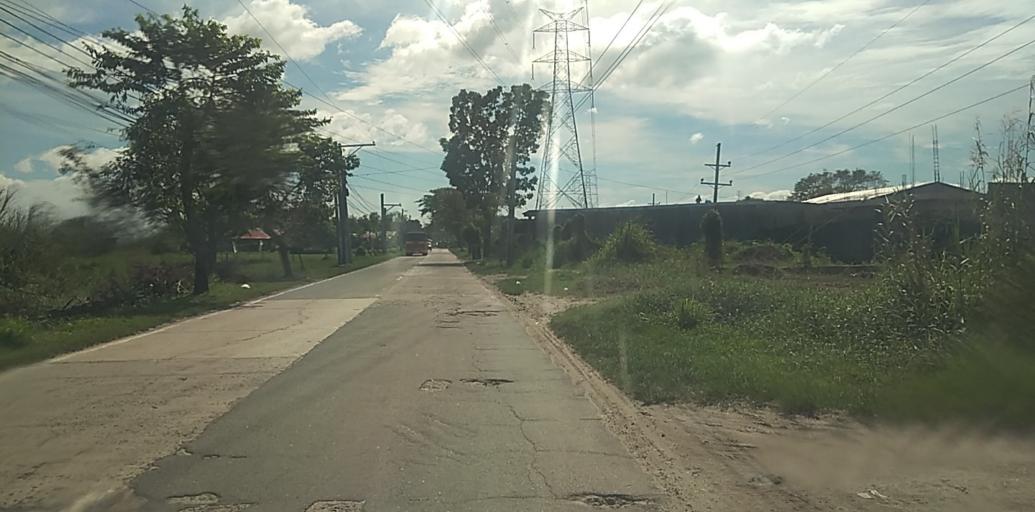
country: PH
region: Central Luzon
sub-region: Province of Pampanga
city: Buensuseso
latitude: 15.1991
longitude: 120.6704
